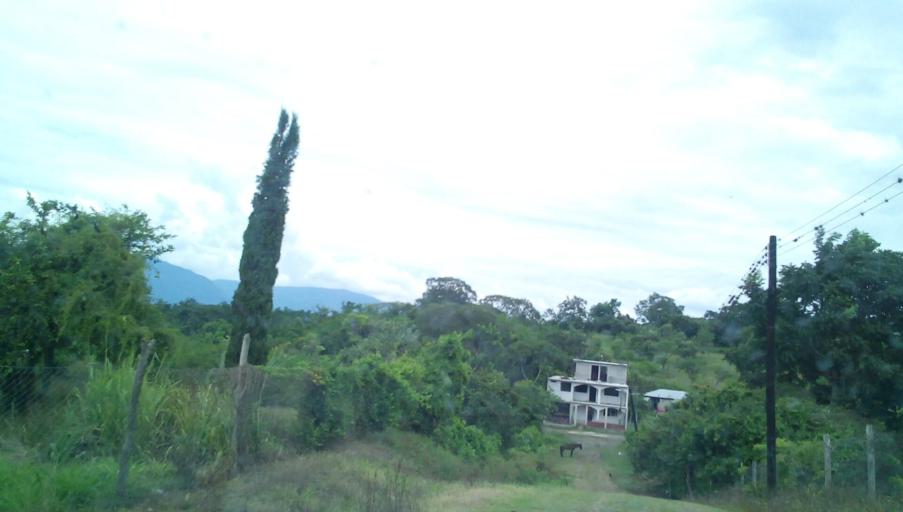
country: MX
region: Veracruz
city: Tepetzintla
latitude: 21.1277
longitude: -97.8556
